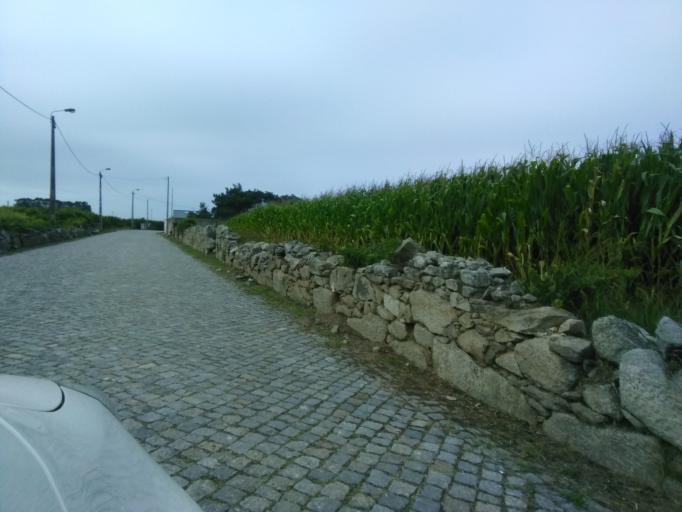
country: PT
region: Porto
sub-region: Matosinhos
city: Lavra
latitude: 41.2429
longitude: -8.7121
